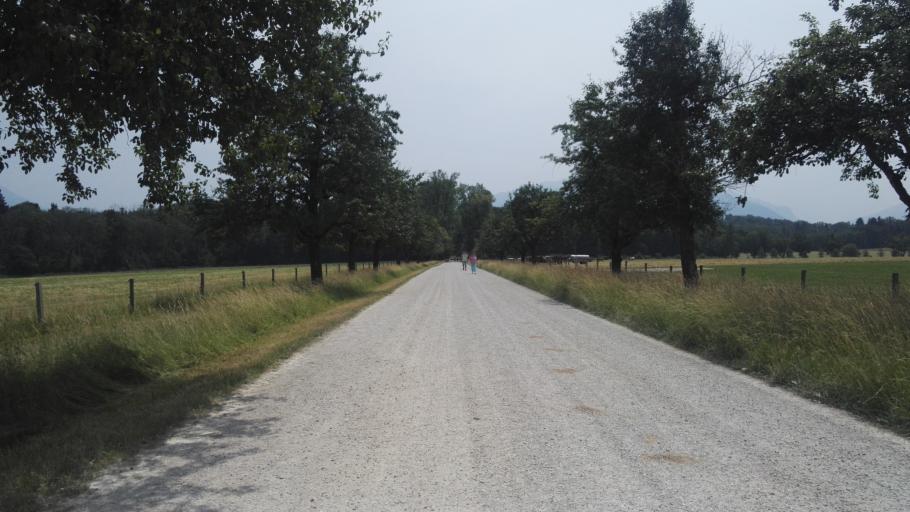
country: DE
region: Bavaria
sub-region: Upper Bavaria
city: Chiemsee
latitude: 47.8653
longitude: 12.3940
